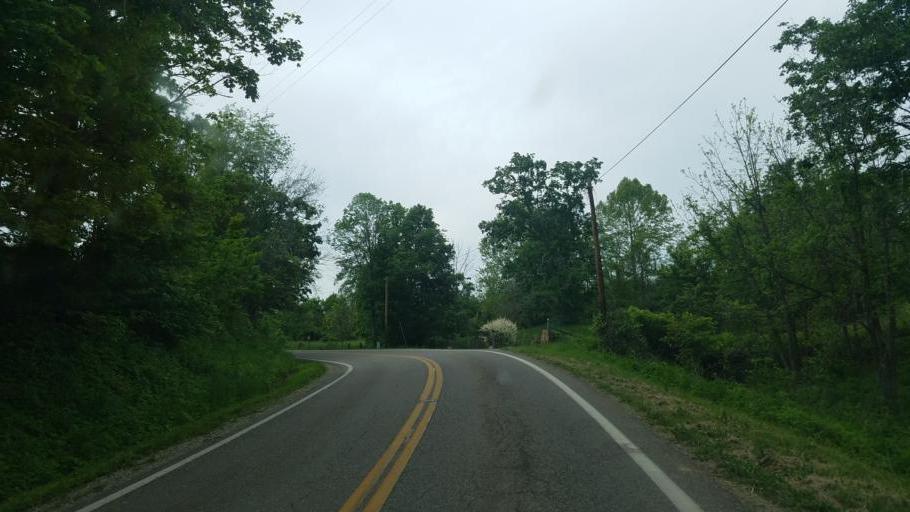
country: US
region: Ohio
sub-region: Athens County
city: Athens
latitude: 39.1629
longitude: -82.2242
